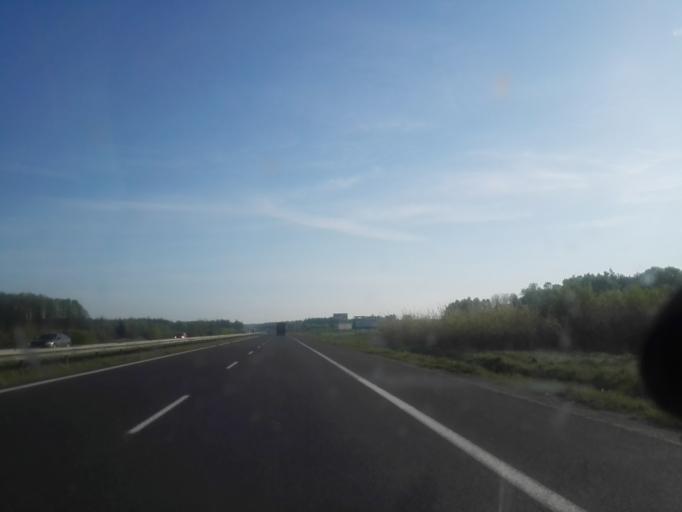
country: PL
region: Lodz Voivodeship
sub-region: Powiat radomszczanski
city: Radomsko
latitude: 51.0484
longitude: 19.3518
